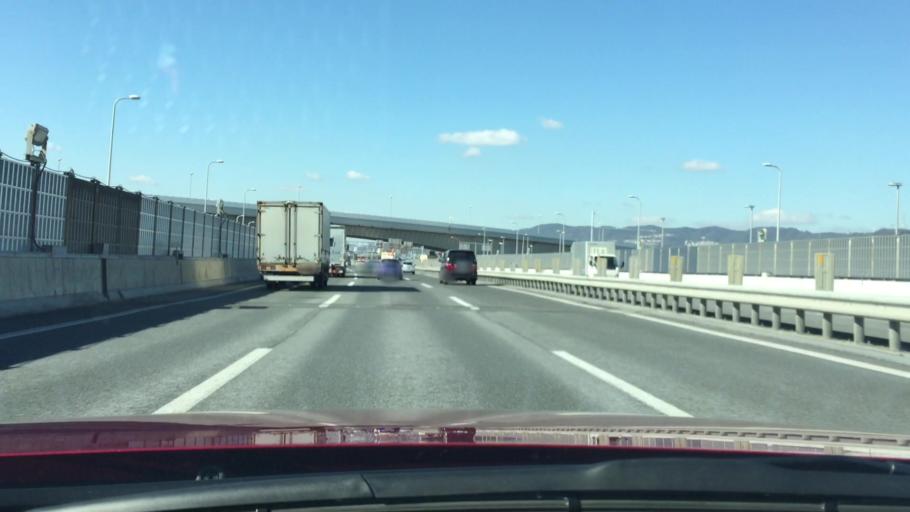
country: JP
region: Hyogo
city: Kawanishi
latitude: 34.8100
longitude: 135.4238
